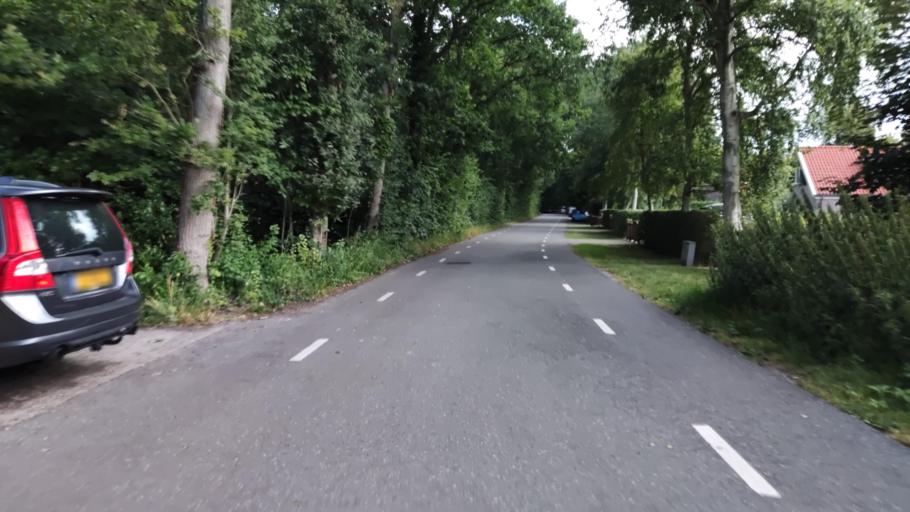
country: NL
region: North Holland
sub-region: Gemeente Texel
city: Den Burg
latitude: 53.0831
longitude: 4.7647
